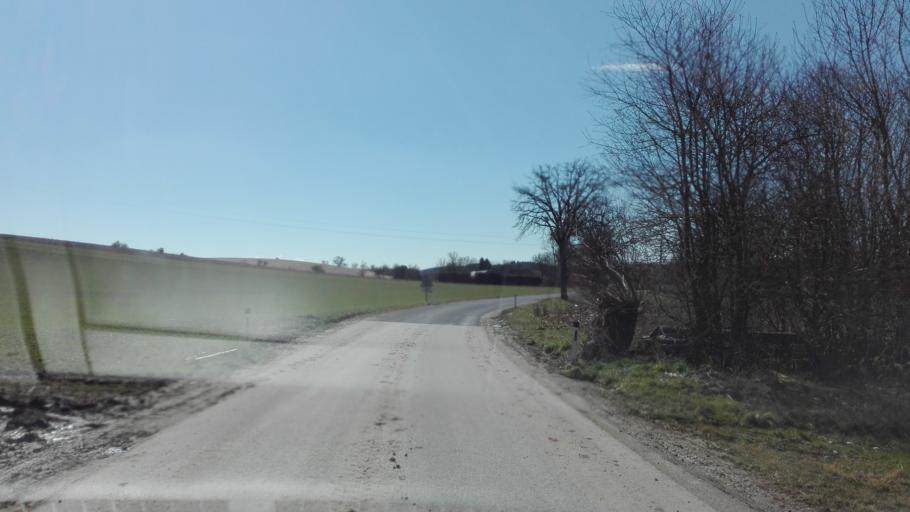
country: AT
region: Upper Austria
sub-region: Wels-Land
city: Buchkirchen
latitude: 48.2257
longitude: 13.9724
